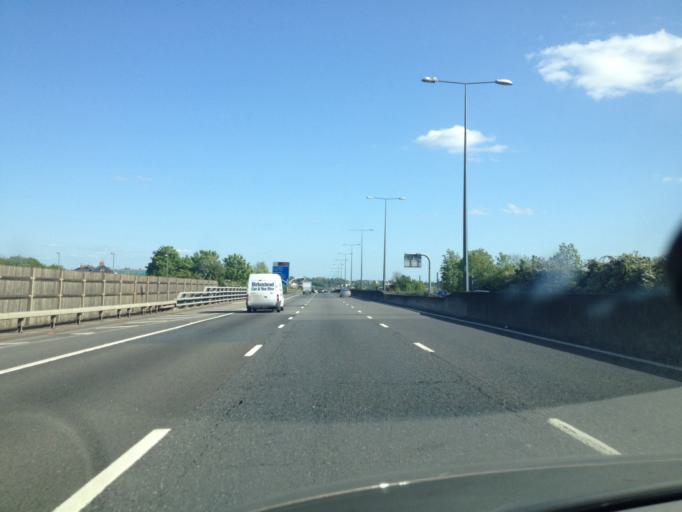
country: GB
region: England
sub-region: Greater London
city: Edgware
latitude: 51.6102
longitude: -0.2457
